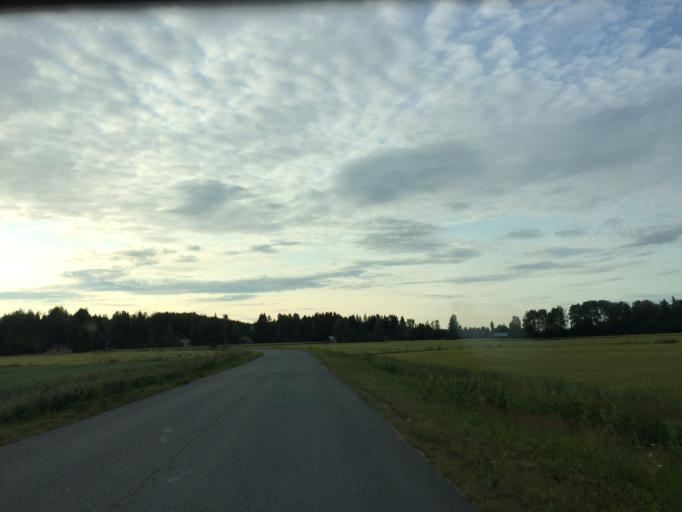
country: FI
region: Haeme
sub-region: Haemeenlinna
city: Tervakoski
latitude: 60.8468
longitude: 24.6266
